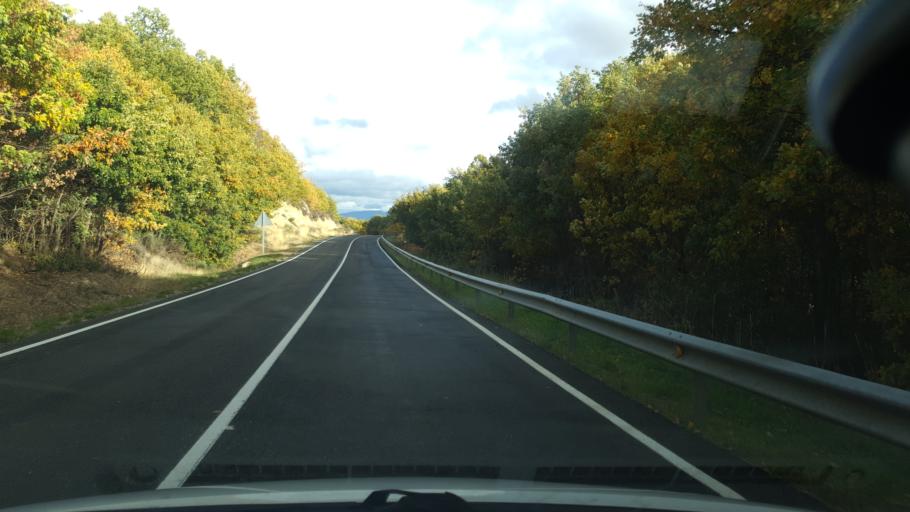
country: ES
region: Castille and Leon
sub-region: Provincia de Avila
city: Hoyocasero
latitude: 40.3947
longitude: -4.9929
